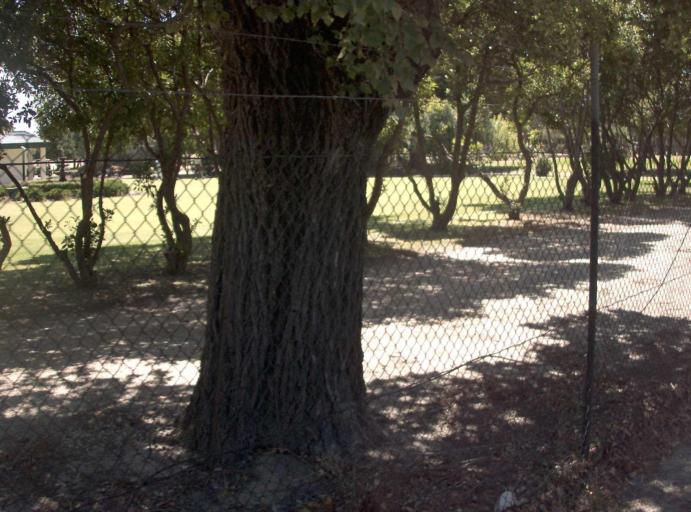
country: AU
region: Victoria
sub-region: Port Phillip
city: St Kilda West
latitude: -37.8480
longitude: 144.9774
